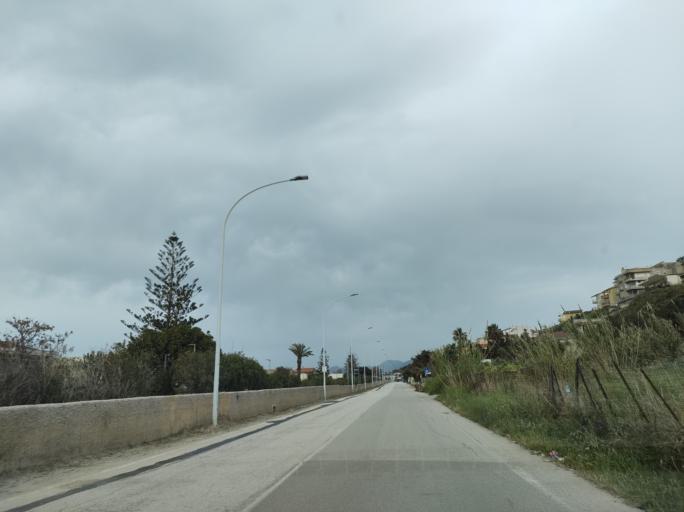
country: IT
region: Sicily
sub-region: Trapani
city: Castellammare del Golfo
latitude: 38.0255
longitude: 12.9219
